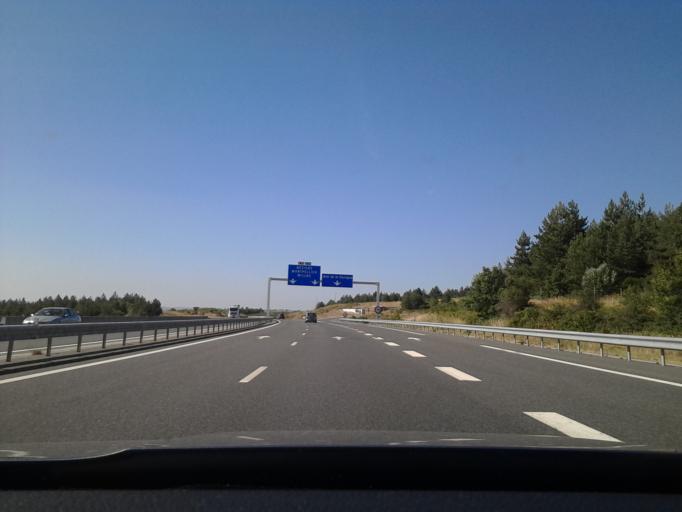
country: FR
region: Midi-Pyrenees
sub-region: Departement de l'Aveyron
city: Millau
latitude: 44.1733
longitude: 3.0315
